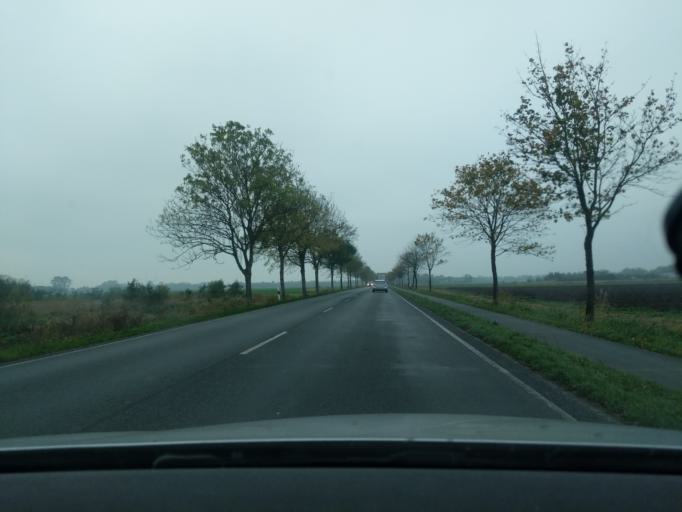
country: DE
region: Lower Saxony
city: Cuxhaven
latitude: 53.8283
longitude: 8.7561
